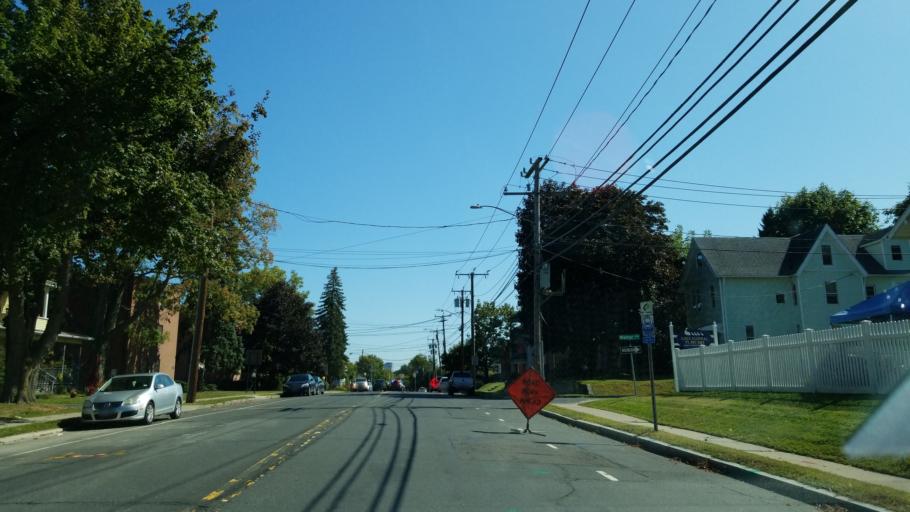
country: US
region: Connecticut
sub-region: Hartford County
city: West Hartford
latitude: 41.7553
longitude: -72.7317
